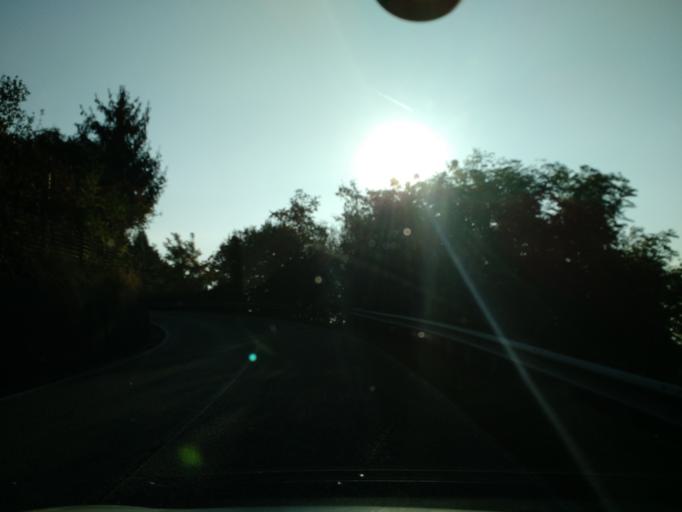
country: IT
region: Veneto
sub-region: Provincia di Vicenza
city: Salcedo
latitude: 45.7699
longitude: 11.5613
